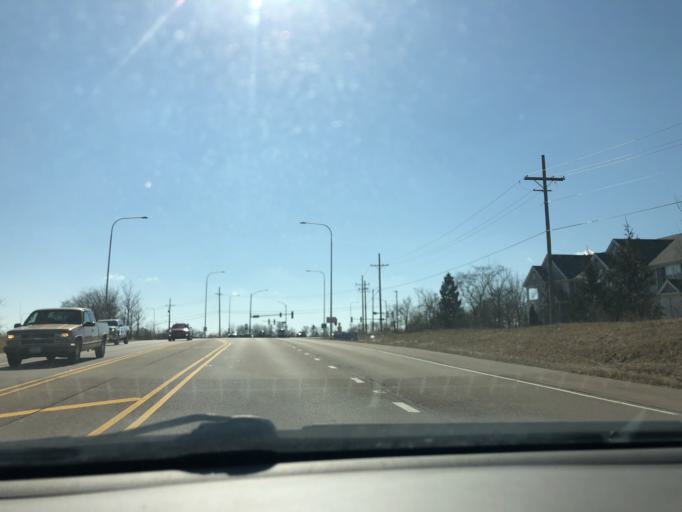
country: US
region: Illinois
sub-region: Kane County
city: Pingree Grove
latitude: 42.0834
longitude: -88.4553
